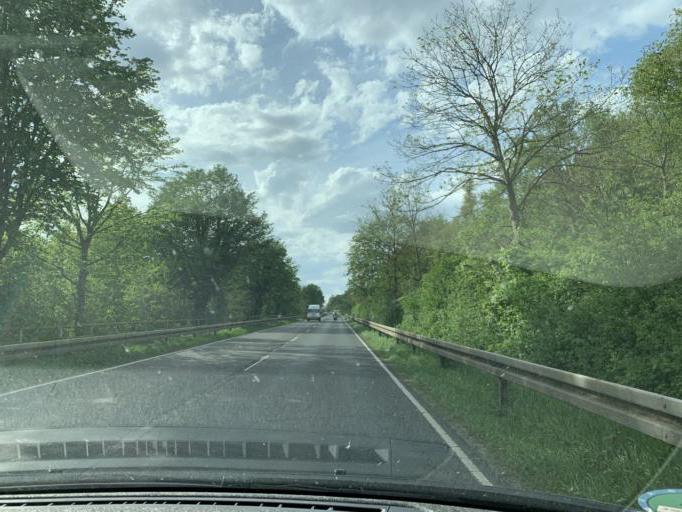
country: DE
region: North Rhine-Westphalia
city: Bruhl
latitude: 50.8365
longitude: 6.8764
